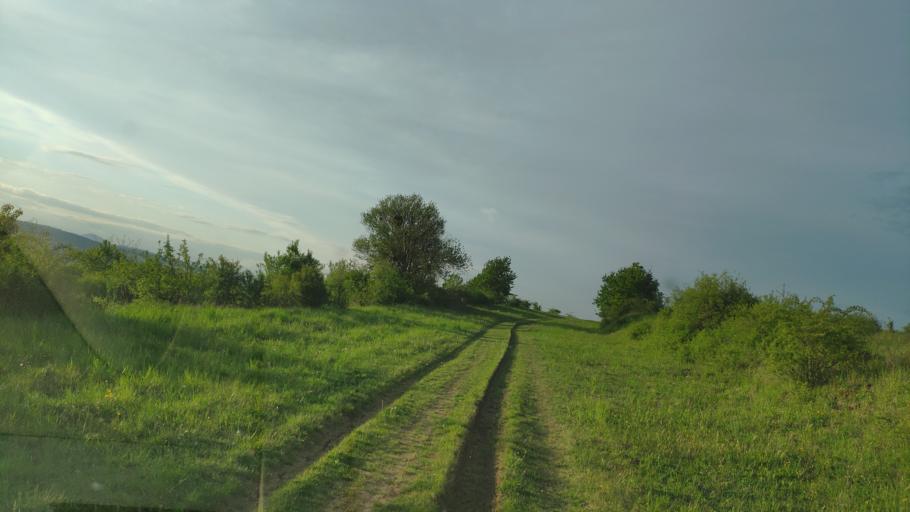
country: SK
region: Kosicky
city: Kosice
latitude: 48.7156
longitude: 21.3544
